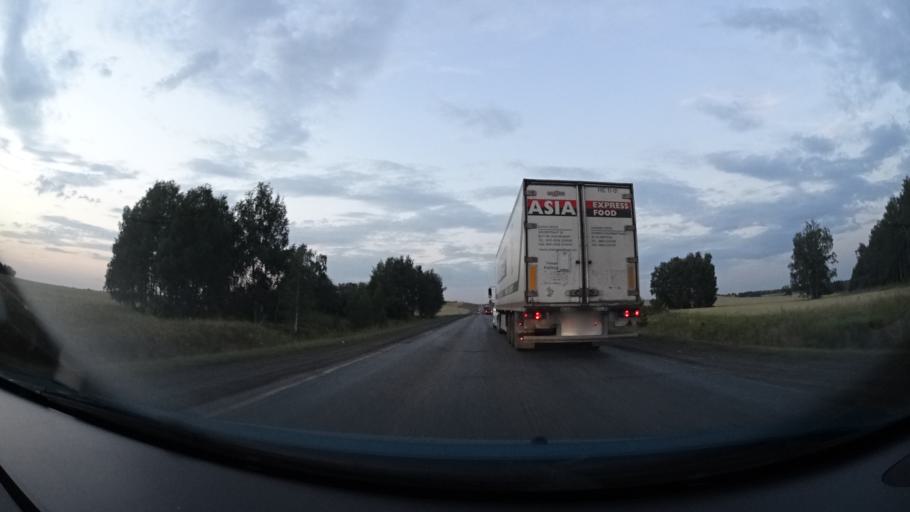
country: RU
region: Tatarstan
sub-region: Bavlinskiy Rayon
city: Bavly
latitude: 54.2886
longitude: 52.9988
